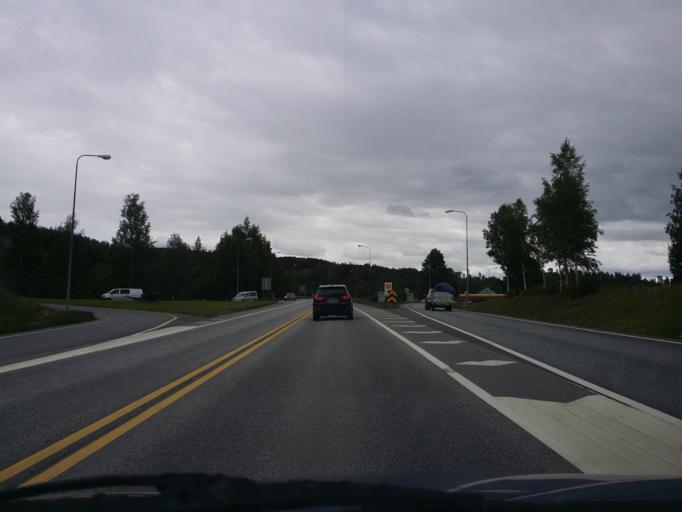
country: NO
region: Hedmark
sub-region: Ringsaker
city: Moelv
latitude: 60.9192
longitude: 10.7016
